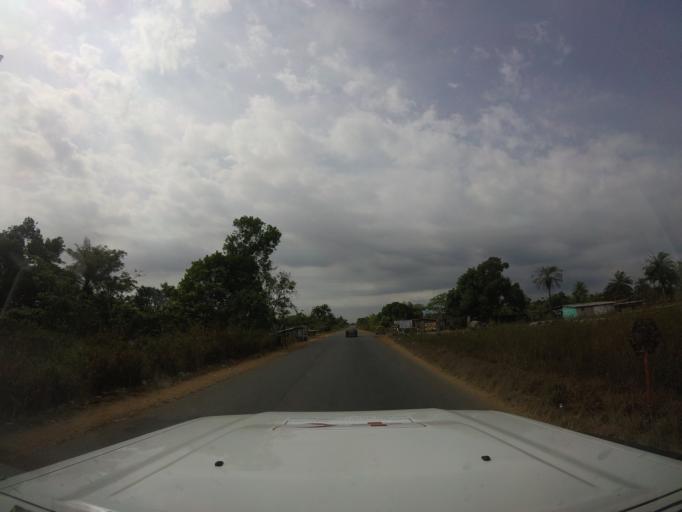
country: LR
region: Montserrado
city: Monrovia
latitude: 6.4706
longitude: -10.8093
